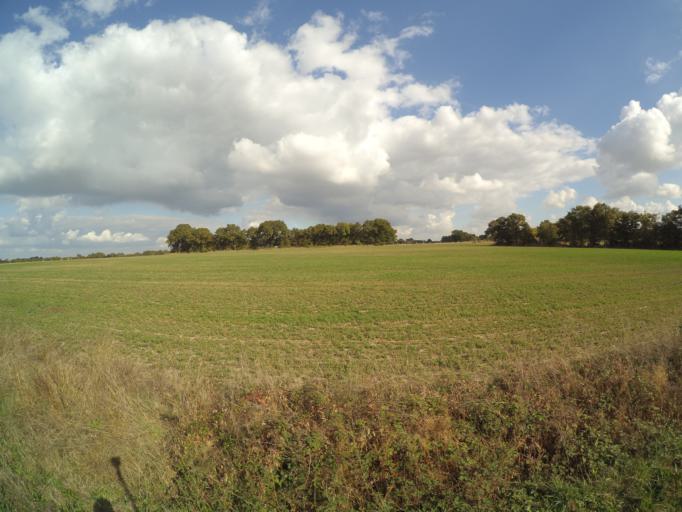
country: FR
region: Pays de la Loire
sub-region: Departement de la Loire-Atlantique
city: Remouille
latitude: 47.0672
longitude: -1.3678
